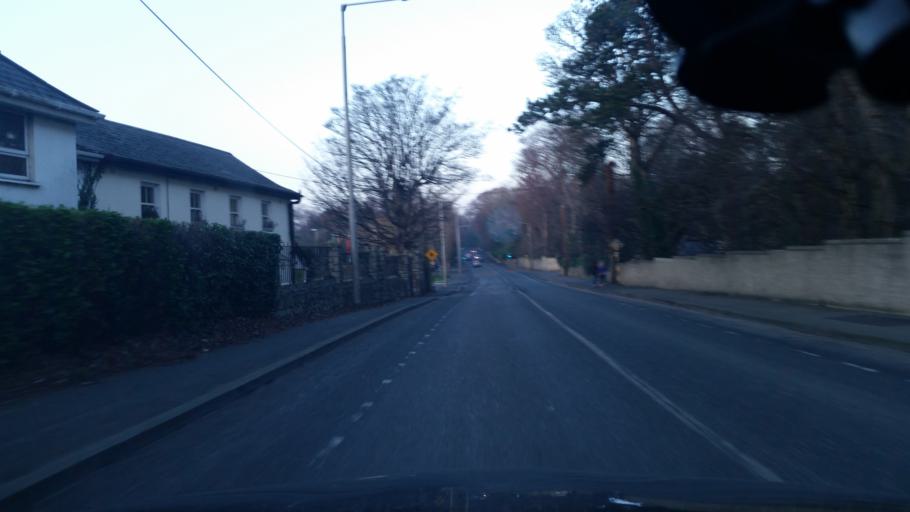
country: IE
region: Leinster
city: Little Bray
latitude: 53.2147
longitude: -6.1195
